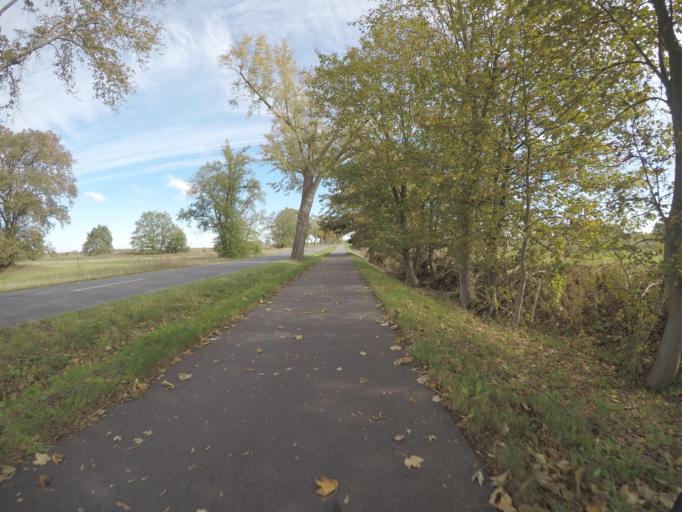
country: DE
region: Brandenburg
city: Stahnsdorf
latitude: 52.3323
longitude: 13.1796
